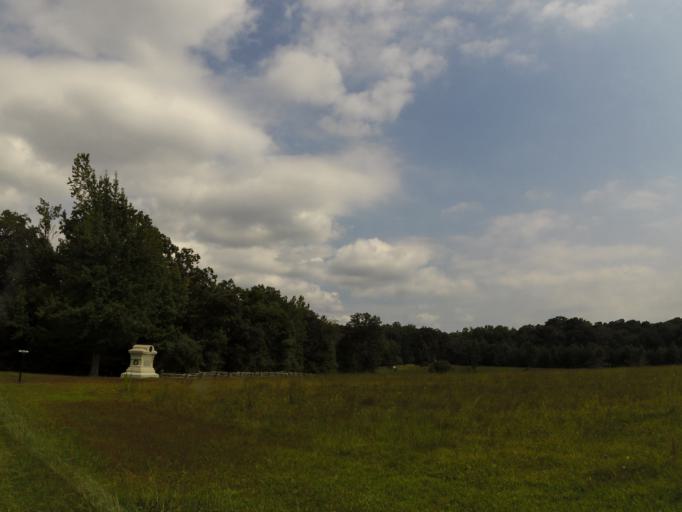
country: US
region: Tennessee
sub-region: Hardin County
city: Crump
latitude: 35.1382
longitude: -88.3407
